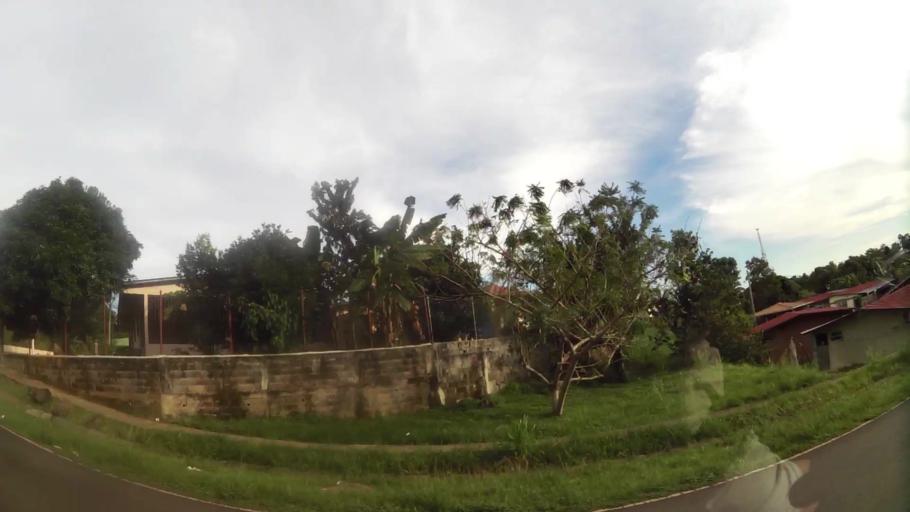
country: PA
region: Panama
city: La Chorrera
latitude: 8.8970
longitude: -79.7662
